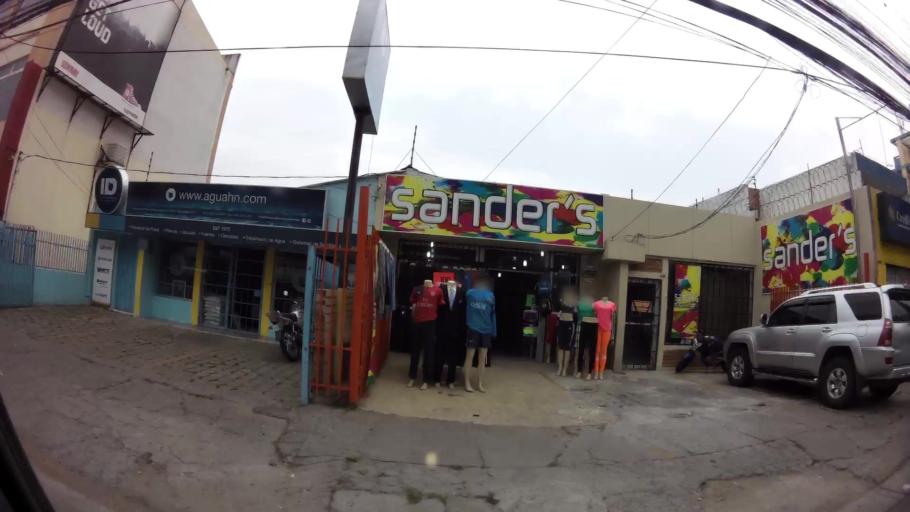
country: HN
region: Francisco Morazan
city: Tegucigalpa
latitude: 14.1012
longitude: -87.1880
